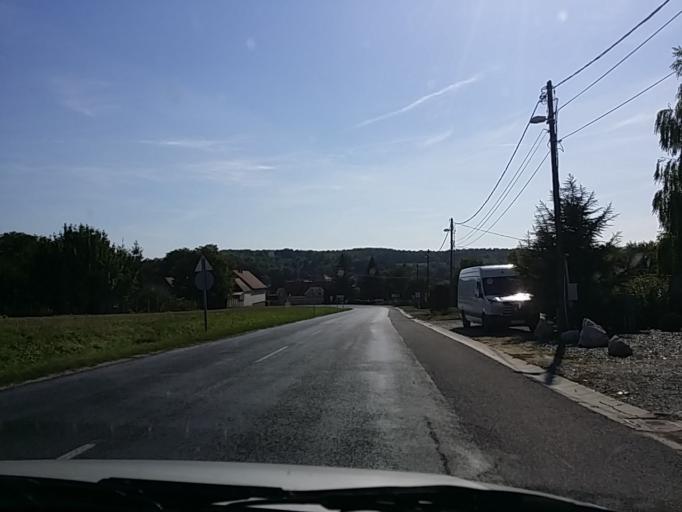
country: AT
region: Burgenland
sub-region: Politischer Bezirk Oberpullendorf
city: Lutzmannsburg
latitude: 47.4282
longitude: 16.6509
